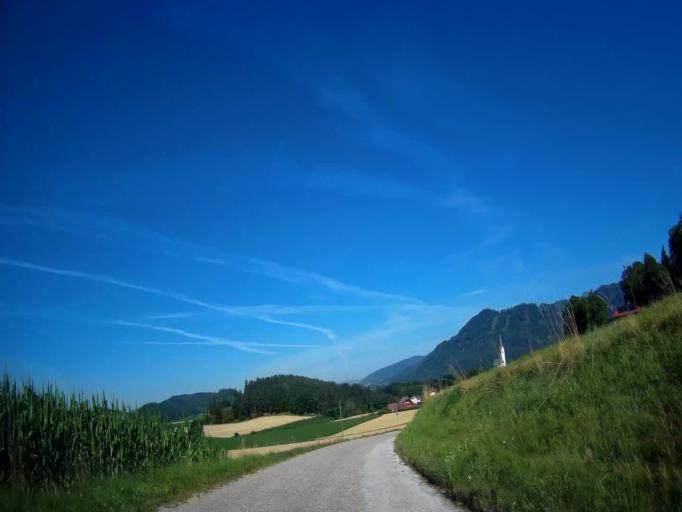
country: AT
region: Carinthia
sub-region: Politischer Bezirk Klagenfurt Land
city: Poggersdorf
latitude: 46.6781
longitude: 14.5086
